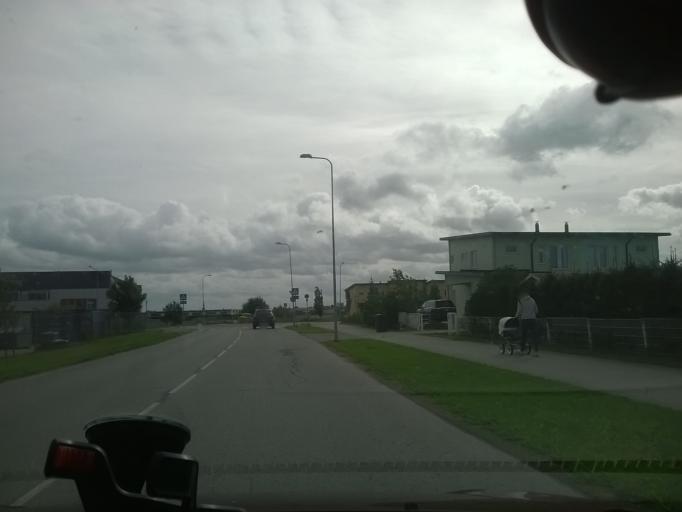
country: EE
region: Harju
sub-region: Tallinna linn
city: Tallinn
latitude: 59.3934
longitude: 24.8161
